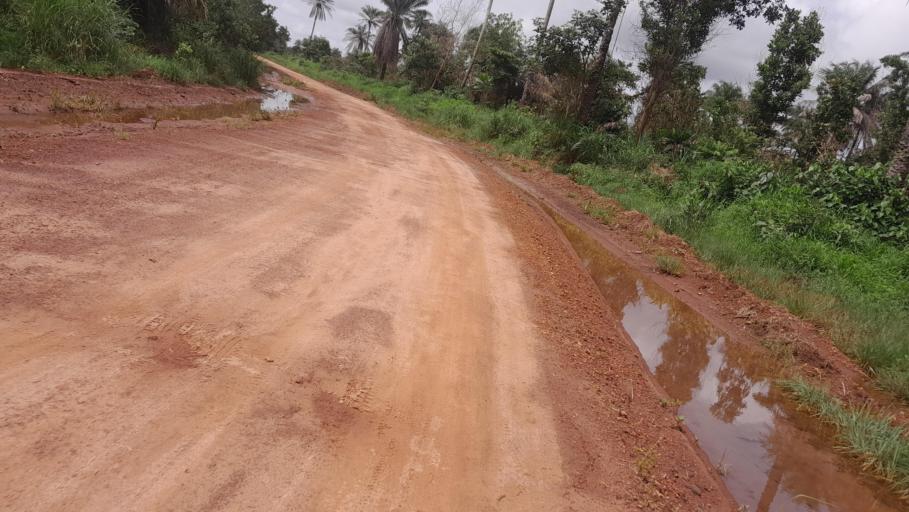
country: GN
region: Boke
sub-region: Boffa
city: Boffa
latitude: 10.0729
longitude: -13.8684
